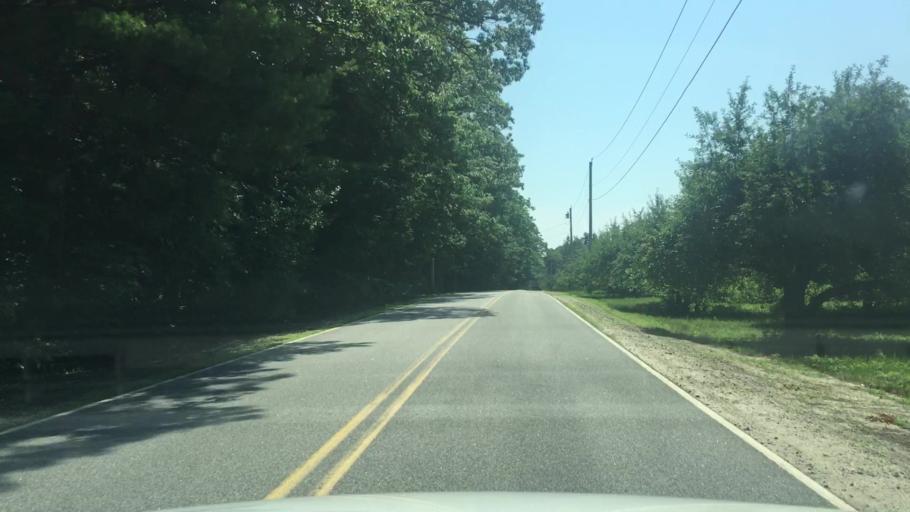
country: US
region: Maine
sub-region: Cumberland County
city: Cumberland Center
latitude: 43.8366
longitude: -70.3064
